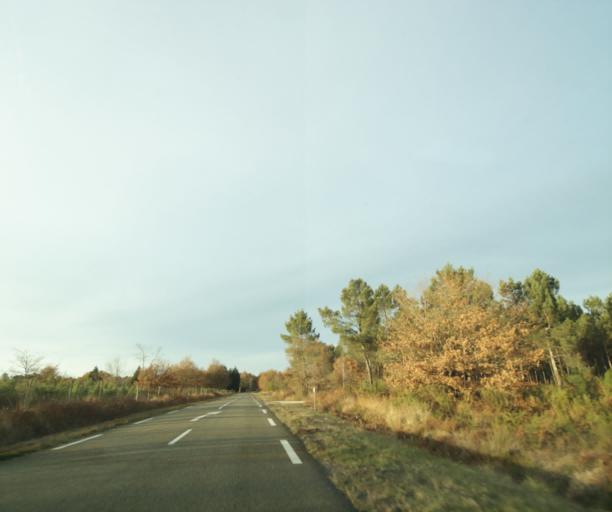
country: FR
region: Aquitaine
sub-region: Departement des Landes
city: Gabarret
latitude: 44.1520
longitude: -0.1287
